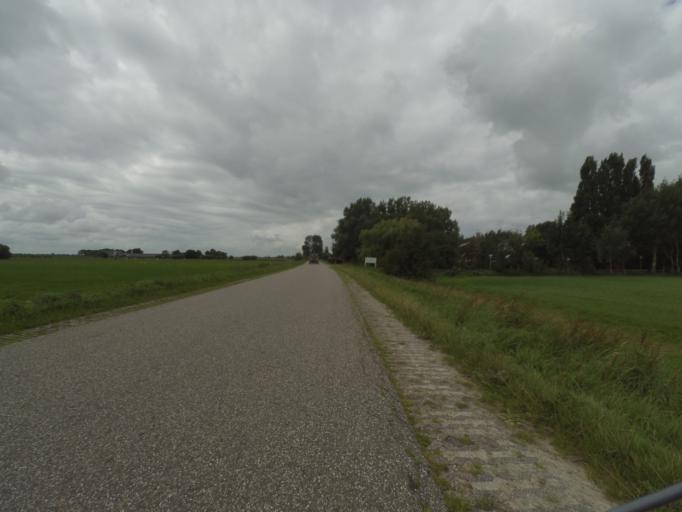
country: NL
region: Friesland
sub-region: Gemeente Dongeradeel
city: Anjum
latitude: 53.3205
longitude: 6.0993
